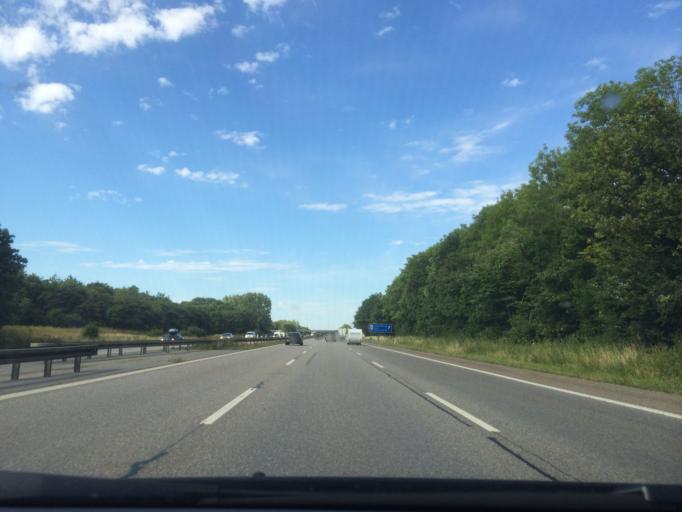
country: DK
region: Capital Region
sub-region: Ishoj Kommune
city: Ishoj
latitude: 55.6221
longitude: 12.3514
